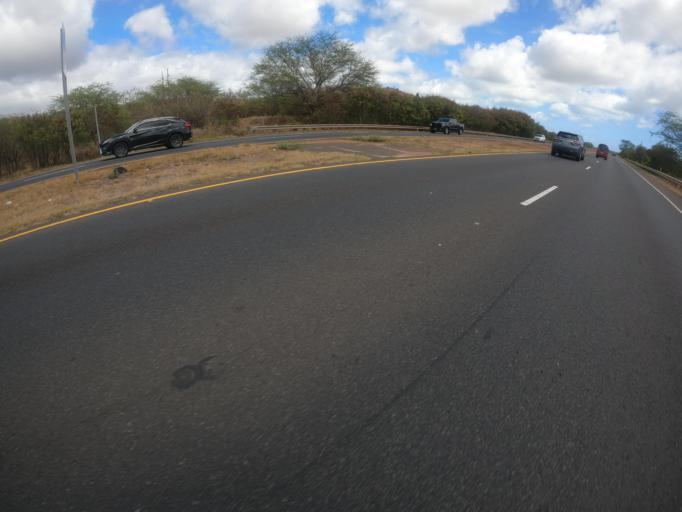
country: US
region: Hawaii
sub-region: Honolulu County
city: Makakilo City
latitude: 21.3394
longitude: -158.1013
